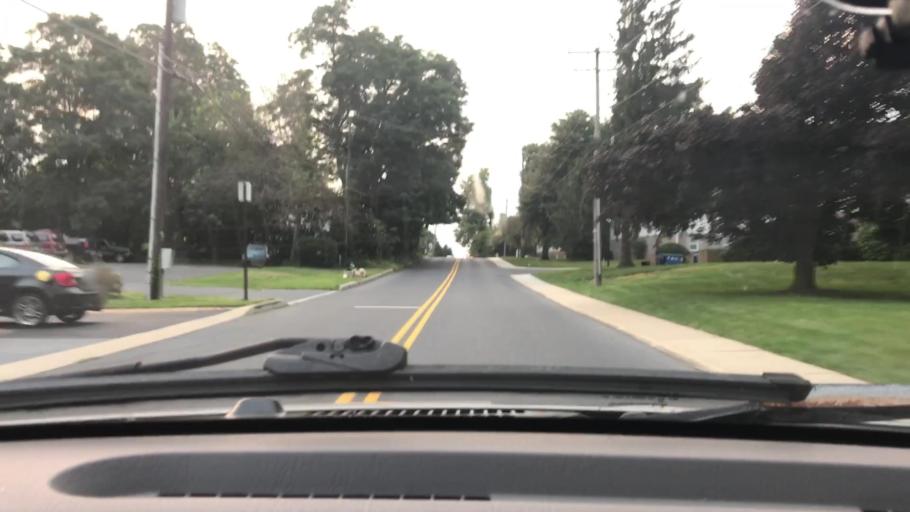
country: US
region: Pennsylvania
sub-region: Lancaster County
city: Elizabethtown
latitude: 40.1627
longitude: -76.5903
